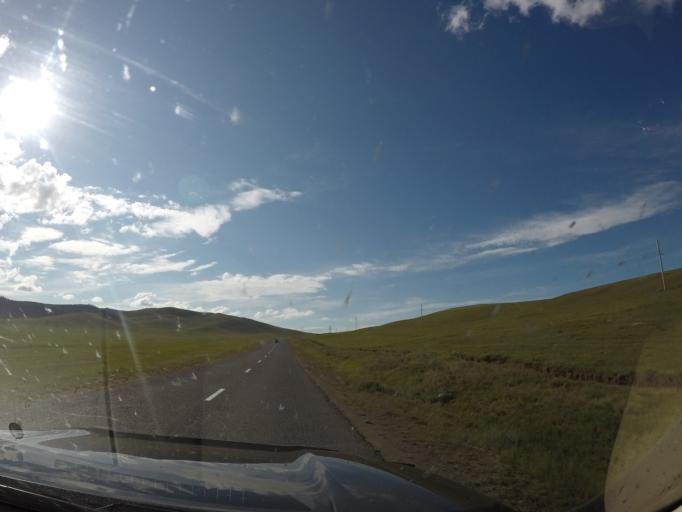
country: MN
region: Hentiy
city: Modot
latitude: 47.7704
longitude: 108.8691
